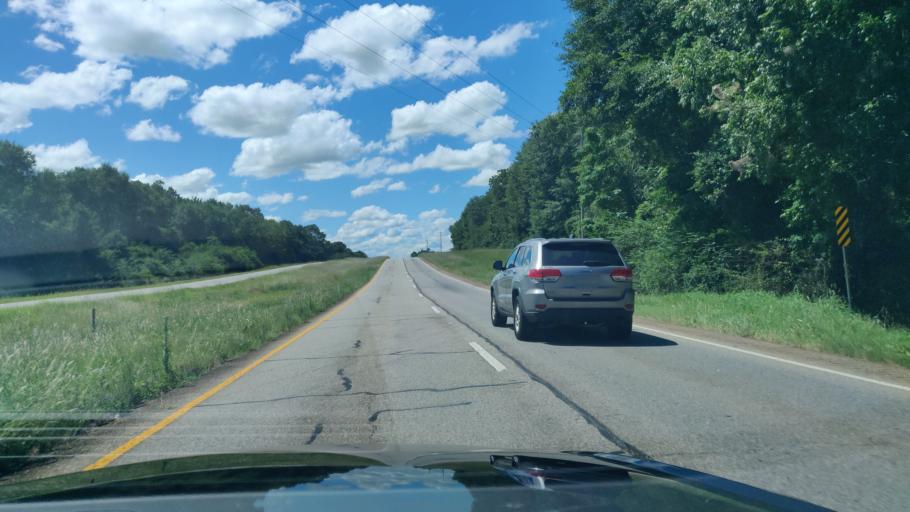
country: US
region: Georgia
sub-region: Webster County
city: Preston
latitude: 31.9254
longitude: -84.5532
